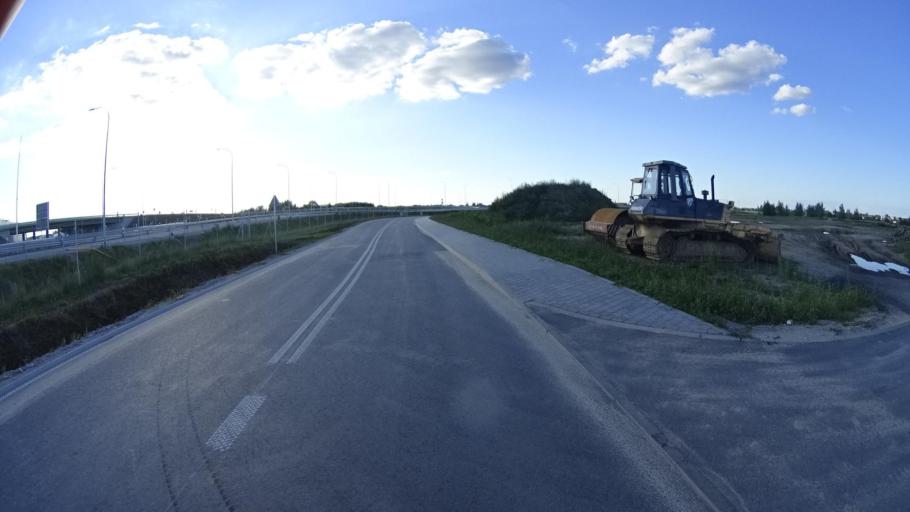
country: PL
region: Masovian Voivodeship
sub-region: Powiat piaseczynski
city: Mysiadlo
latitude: 52.1169
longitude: 20.9883
